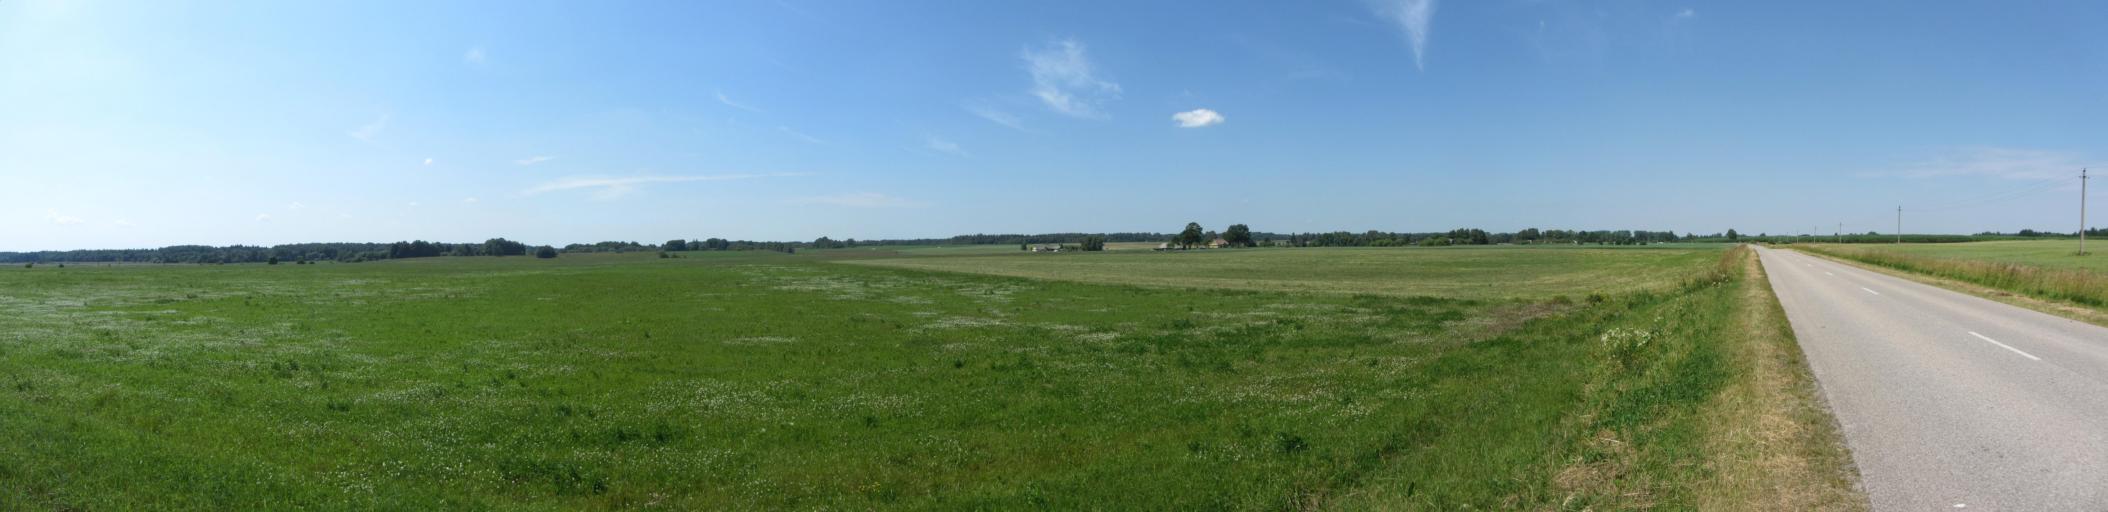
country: LT
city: Sirvintos
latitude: 55.1901
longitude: 24.9535
